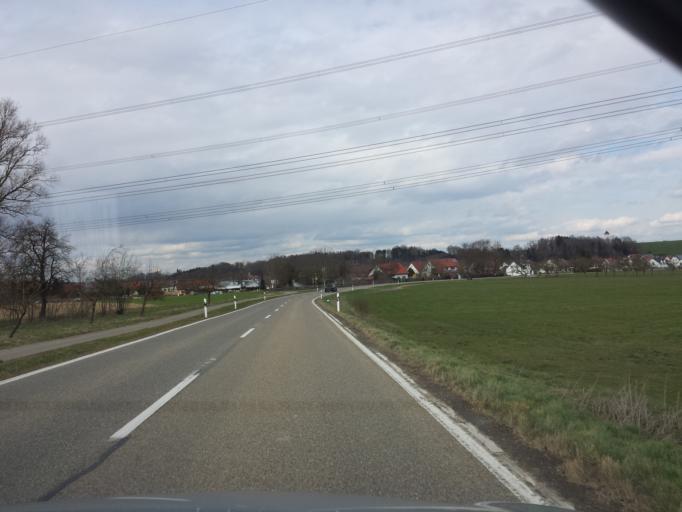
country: DE
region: Baden-Wuerttemberg
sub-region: Tuebingen Region
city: Huttisheim
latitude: 48.2739
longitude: 9.9384
